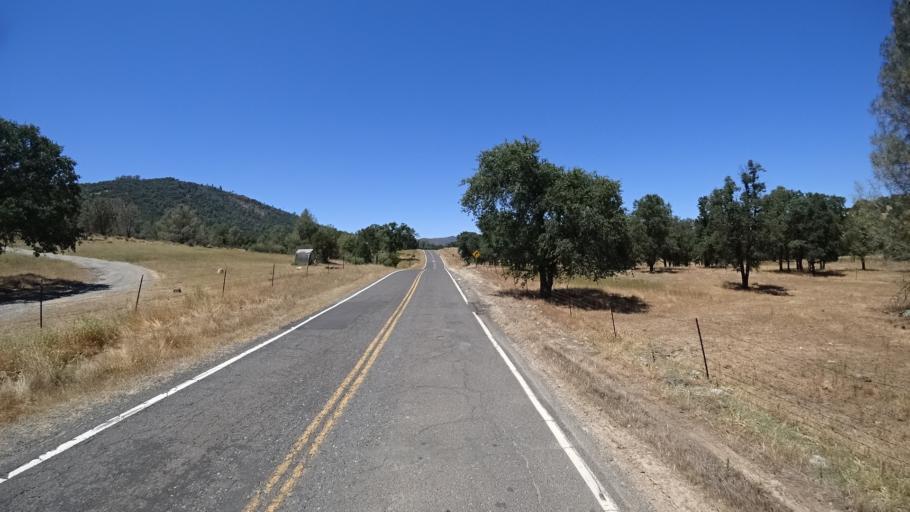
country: US
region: California
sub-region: Calaveras County
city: Copperopolis
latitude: 38.0687
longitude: -120.6595
